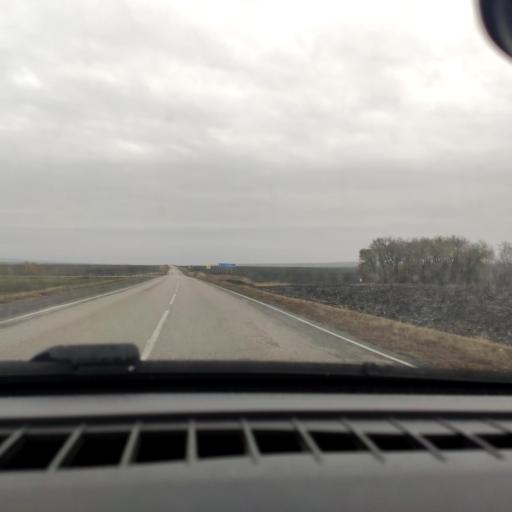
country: RU
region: Belgorod
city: Ilovka
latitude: 50.7778
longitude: 38.8142
